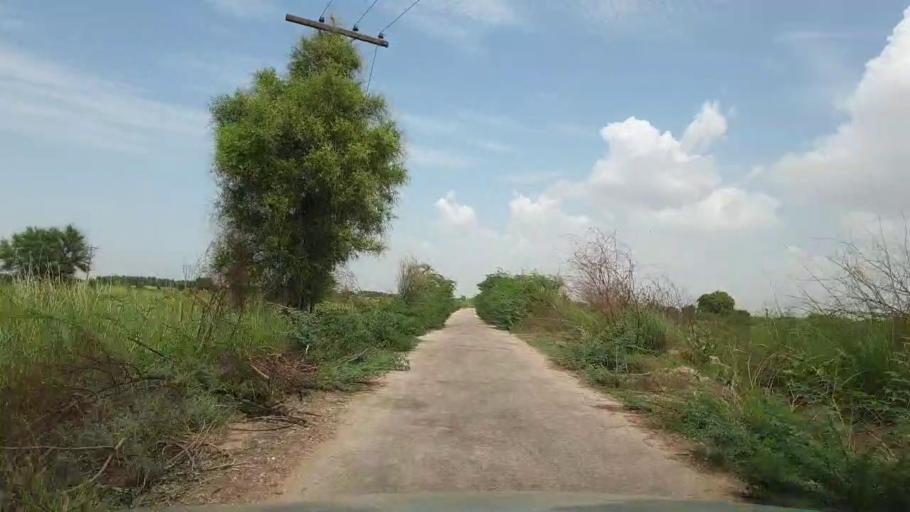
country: PK
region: Sindh
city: Bozdar
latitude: 27.0169
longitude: 68.9417
